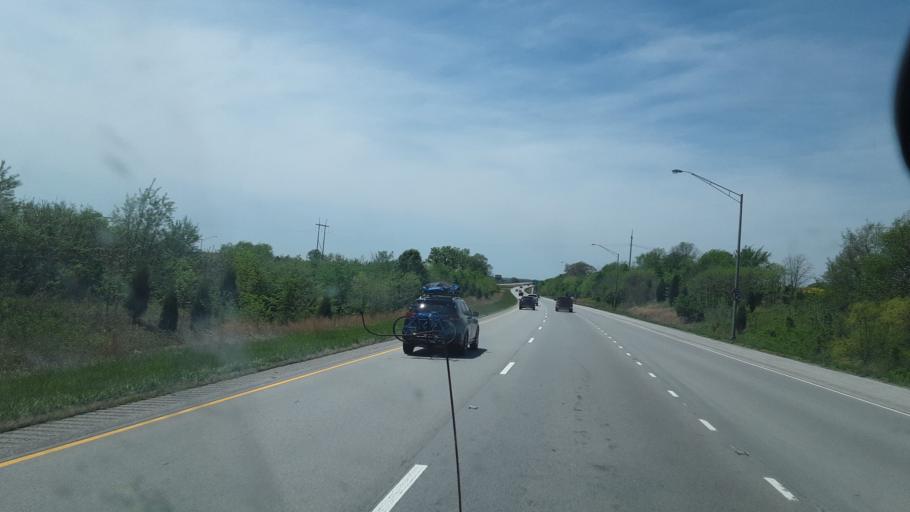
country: US
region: Indiana
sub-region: Spencer County
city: Dale
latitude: 38.1963
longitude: -86.9516
